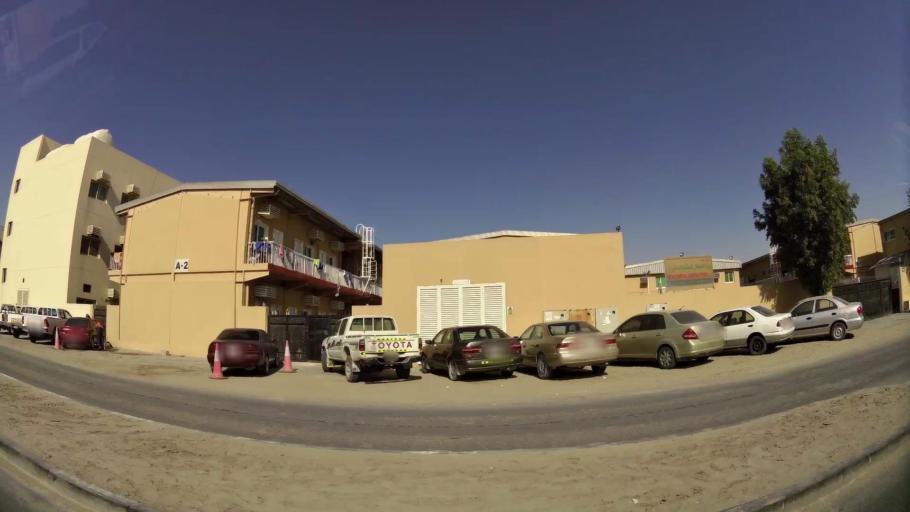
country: AE
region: Dubai
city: Dubai
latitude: 25.0026
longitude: 55.1060
